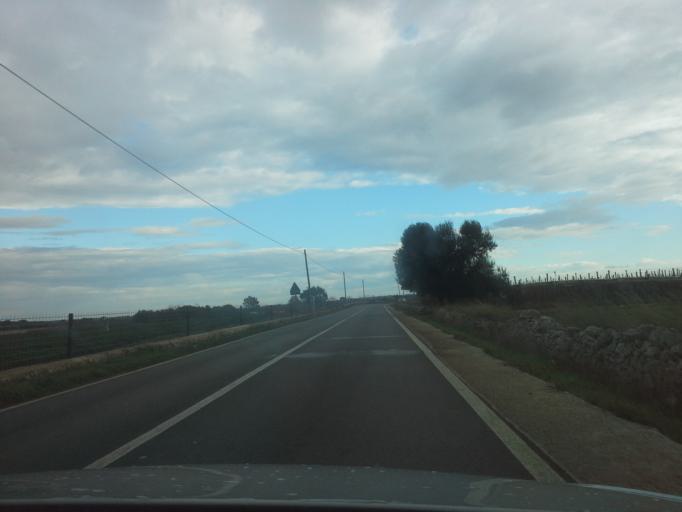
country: IT
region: Apulia
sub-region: Provincia di Bari
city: Casamassima
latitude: 40.9386
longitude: 16.9657
